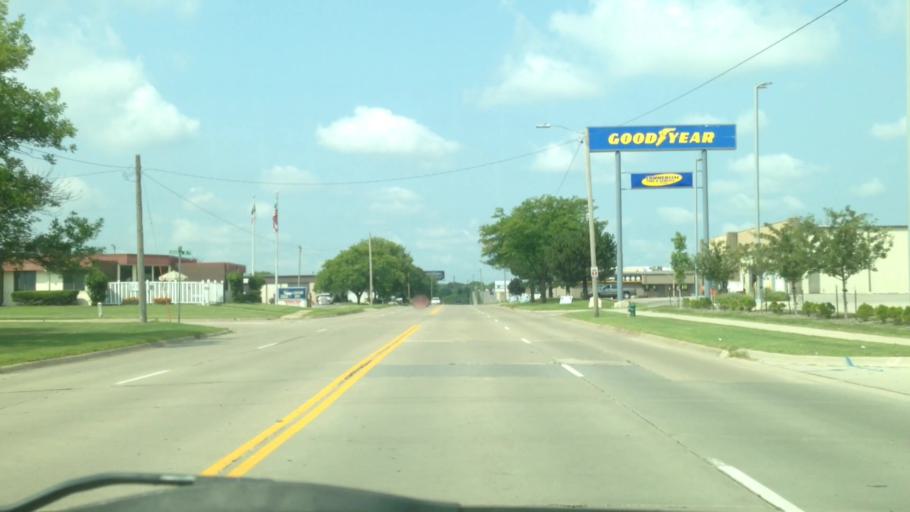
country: US
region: Iowa
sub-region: Linn County
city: Cedar Rapids
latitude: 41.9431
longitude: -91.6796
